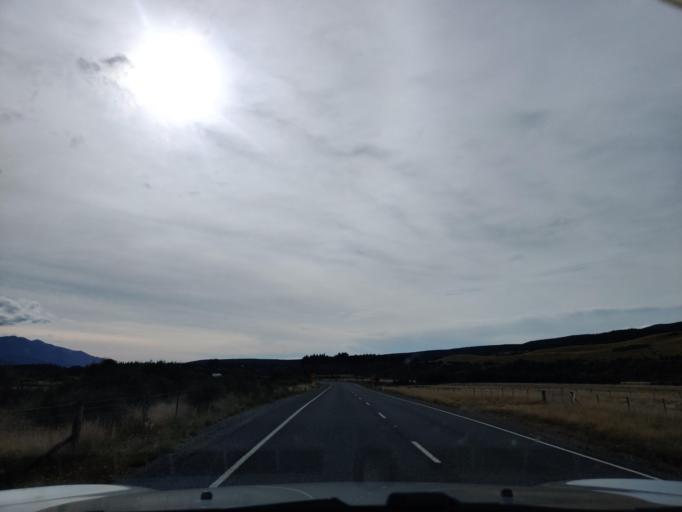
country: NZ
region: Tasman
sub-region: Tasman District
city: Brightwater
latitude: -41.6839
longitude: 173.1657
